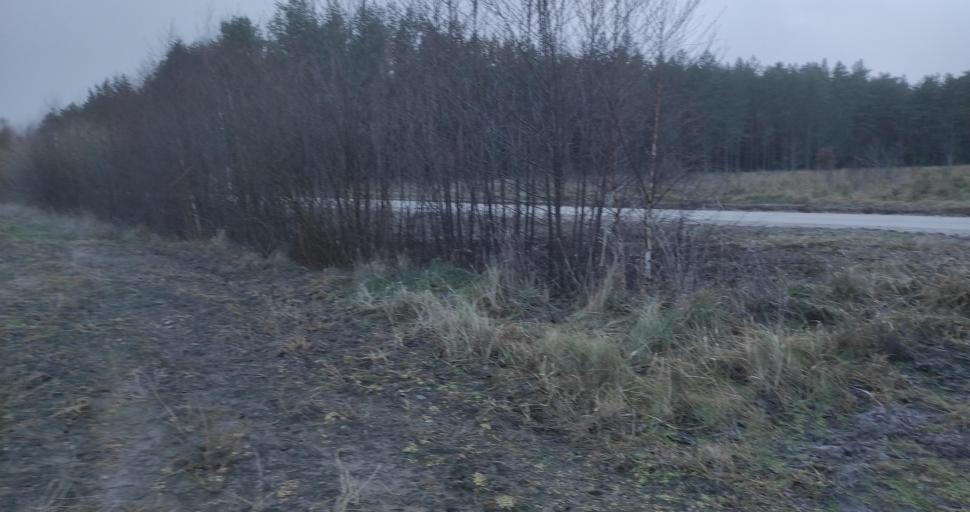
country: LV
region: Pavilostas
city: Pavilosta
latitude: 56.7826
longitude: 21.0728
